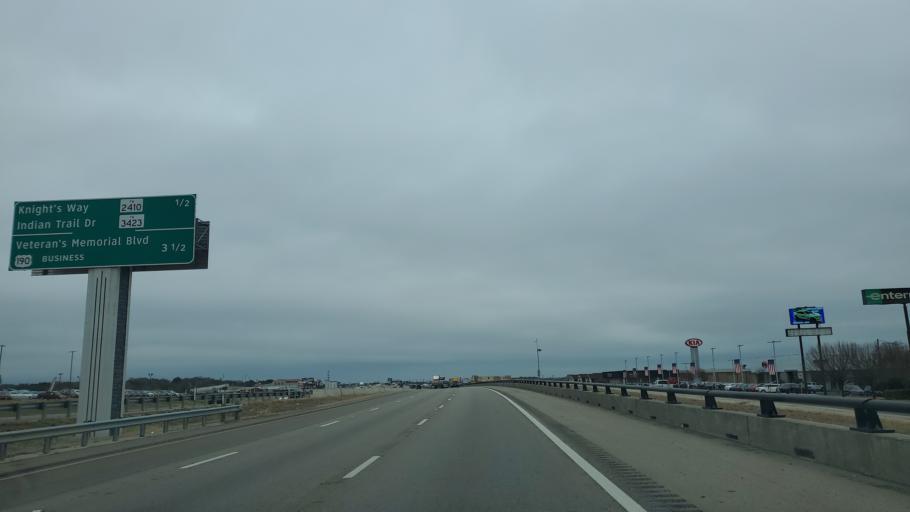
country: US
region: Texas
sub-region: Bell County
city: Harker Heights
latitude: 31.0779
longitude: -97.6939
